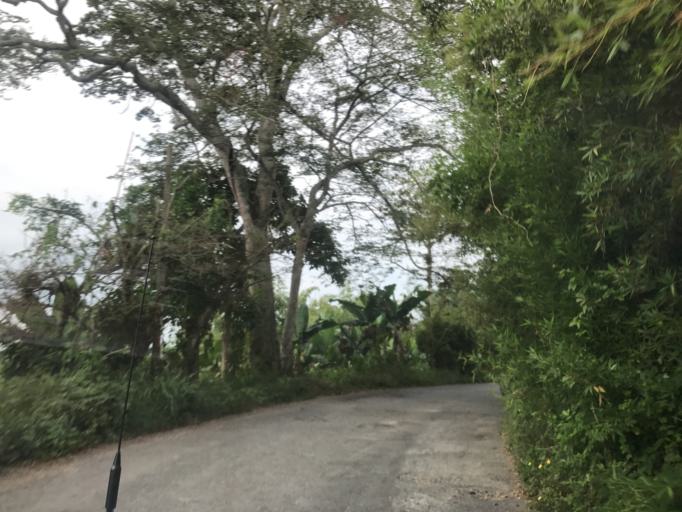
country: CO
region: Quindio
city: Montenegro
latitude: 4.5480
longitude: -75.8093
